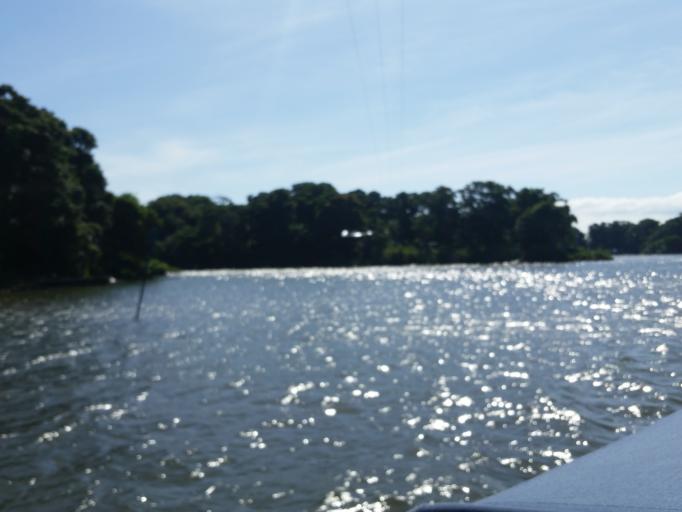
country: NI
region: Granada
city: Granada
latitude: 11.8981
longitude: -85.8955
